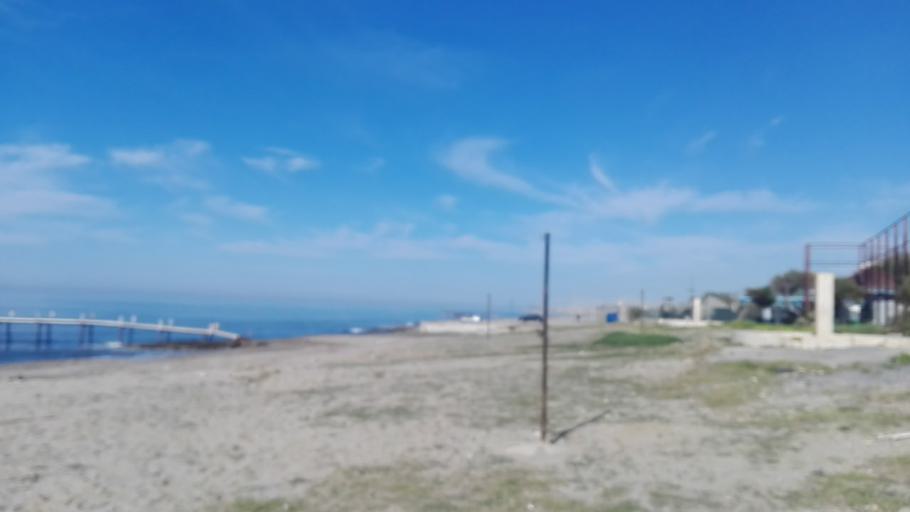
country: TR
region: Antalya
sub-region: Alanya
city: Payallar
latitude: 36.5787
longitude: 31.8827
